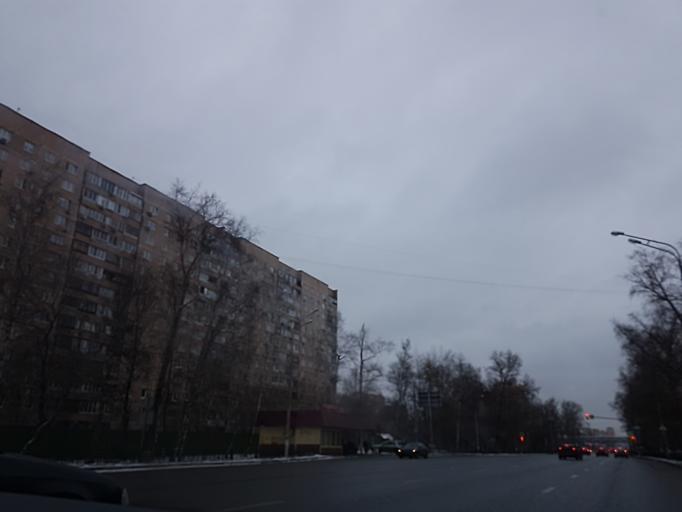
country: RU
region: Moskovskaya
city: Krasnogorsk
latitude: 55.8043
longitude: 37.3247
